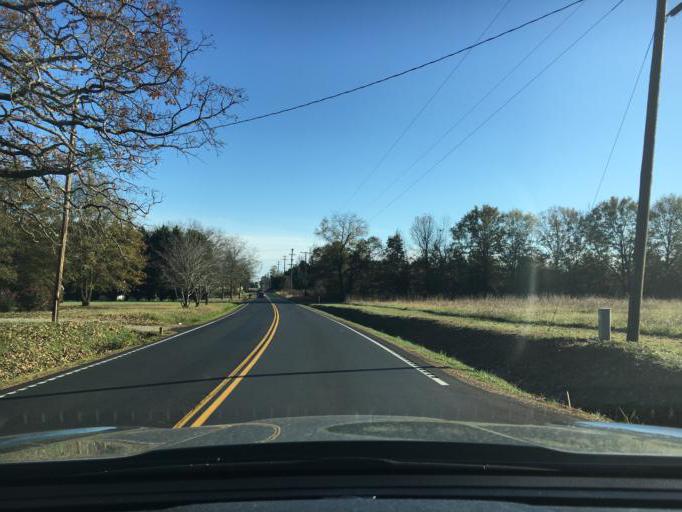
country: US
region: South Carolina
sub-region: Spartanburg County
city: Inman
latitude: 35.0086
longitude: -82.0740
